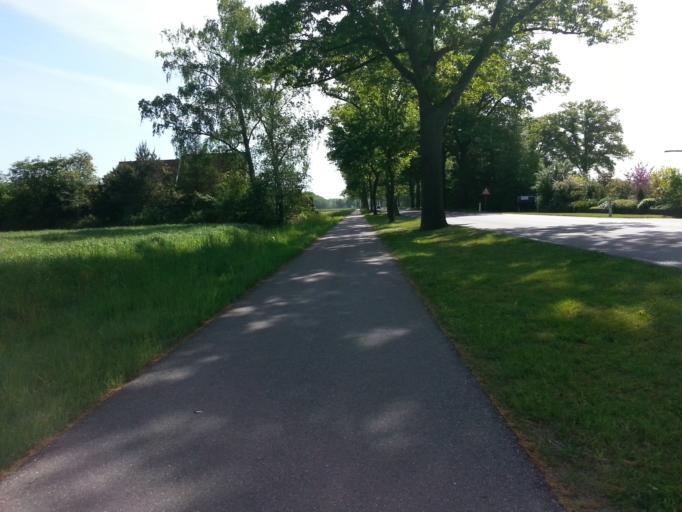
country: NL
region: Gelderland
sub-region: Berkelland
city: Eibergen
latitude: 52.1351
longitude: 6.6630
